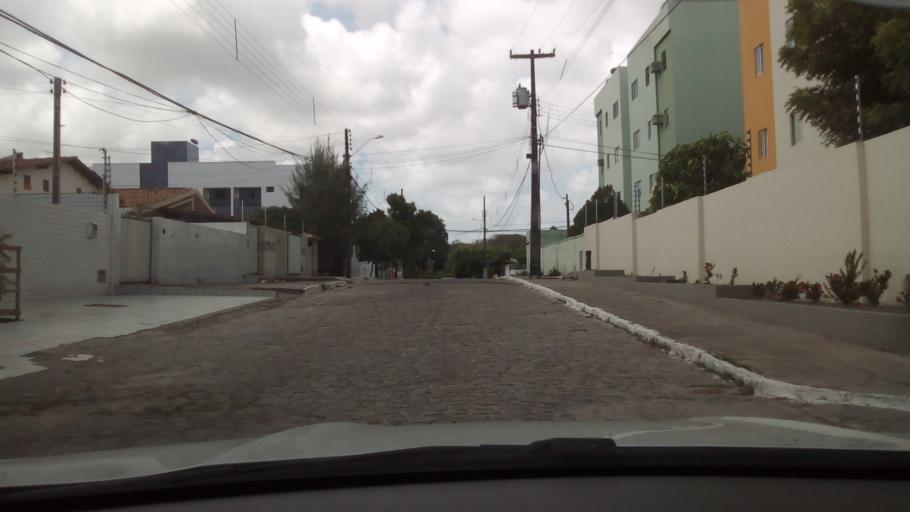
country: BR
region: Paraiba
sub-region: Joao Pessoa
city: Joao Pessoa
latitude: -7.1443
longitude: -34.8361
